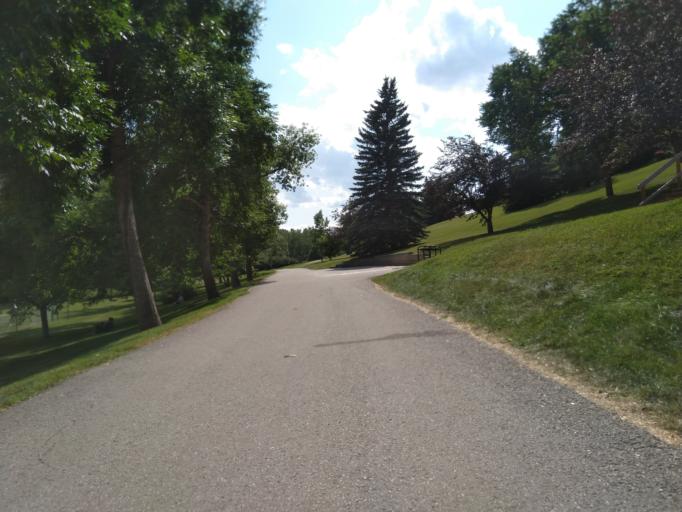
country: CA
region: Alberta
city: Calgary
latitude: 51.0788
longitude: -114.0816
